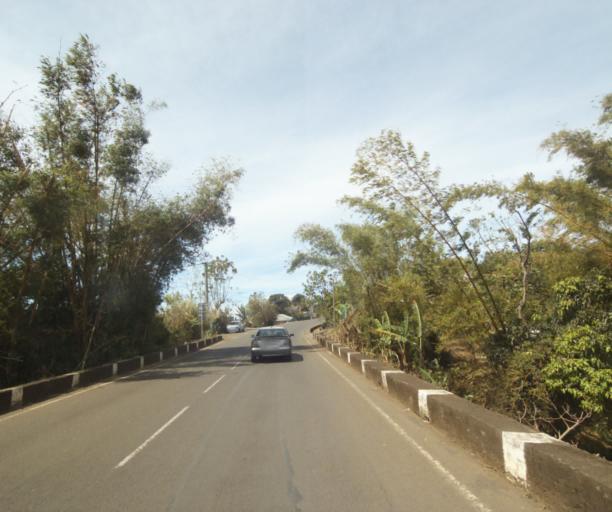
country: RE
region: Reunion
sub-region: Reunion
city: Saint-Paul
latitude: -21.0383
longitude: 55.3060
